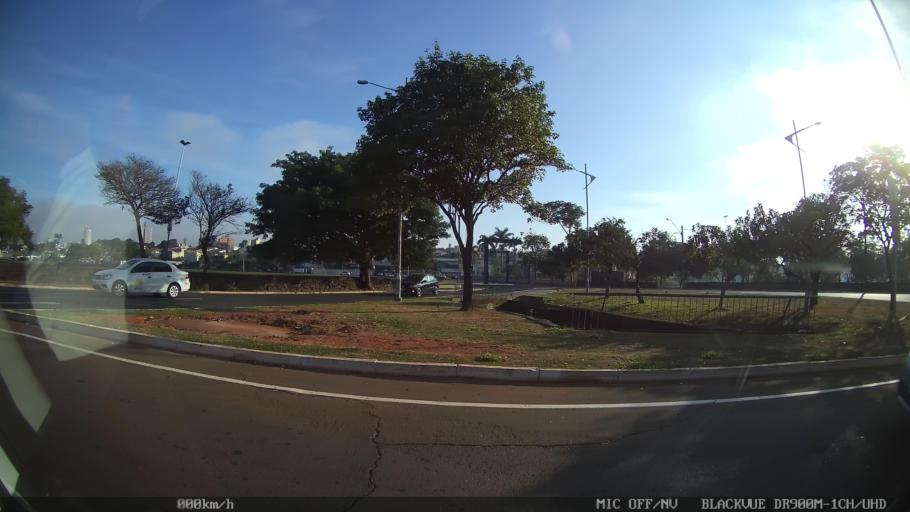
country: BR
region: Sao Paulo
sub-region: Sao Jose Do Rio Preto
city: Sao Jose do Rio Preto
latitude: -20.8099
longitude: -49.3675
